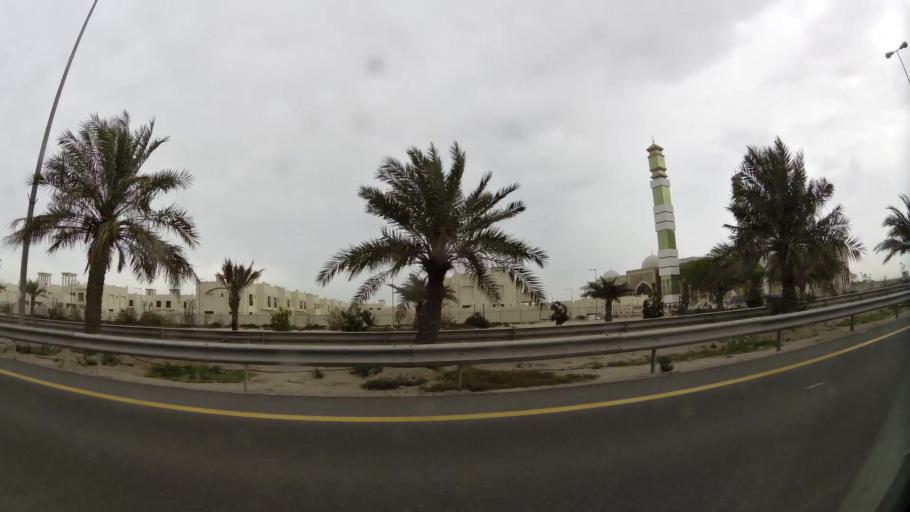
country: BH
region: Central Governorate
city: Dar Kulayb
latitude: 26.0871
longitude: 50.5395
